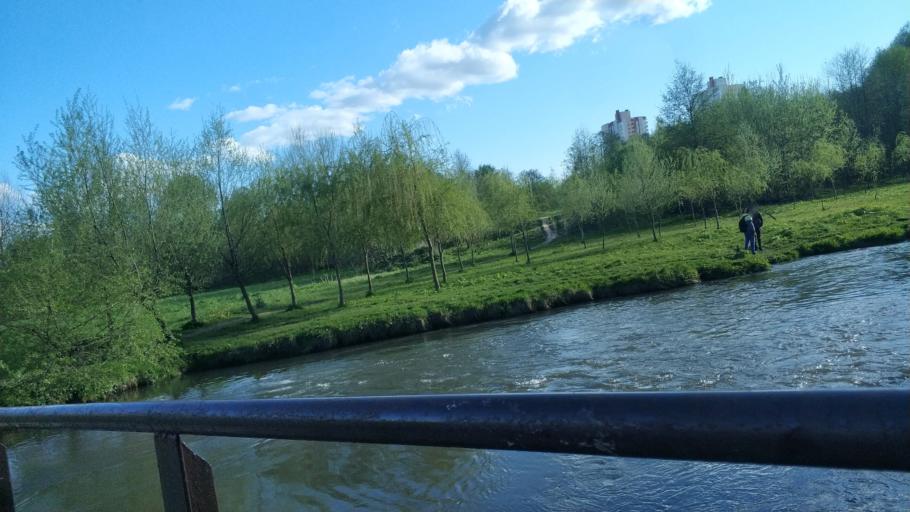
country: BY
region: Minsk
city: Minsk
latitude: 53.8698
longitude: 27.5801
